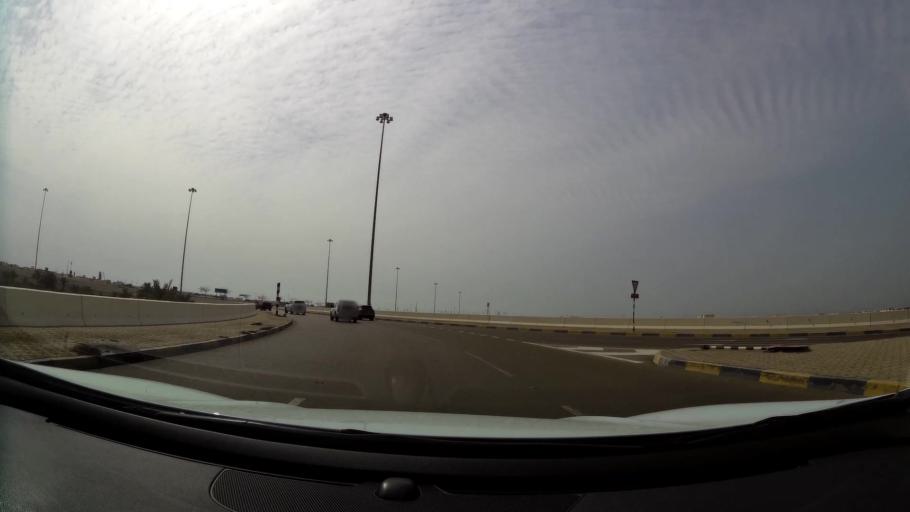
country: AE
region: Abu Dhabi
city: Abu Dhabi
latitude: 24.5650
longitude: 54.6951
